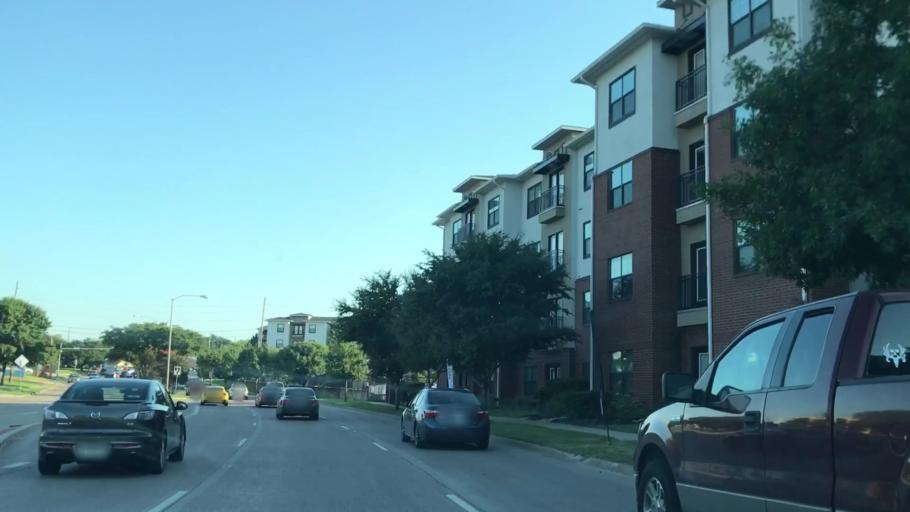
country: US
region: Texas
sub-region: Denton County
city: Denton
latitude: 33.2062
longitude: -97.1367
